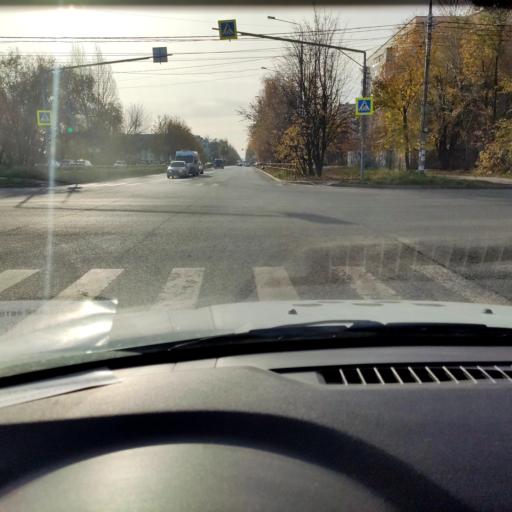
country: RU
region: Samara
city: Tol'yatti
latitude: 53.5401
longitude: 49.4090
